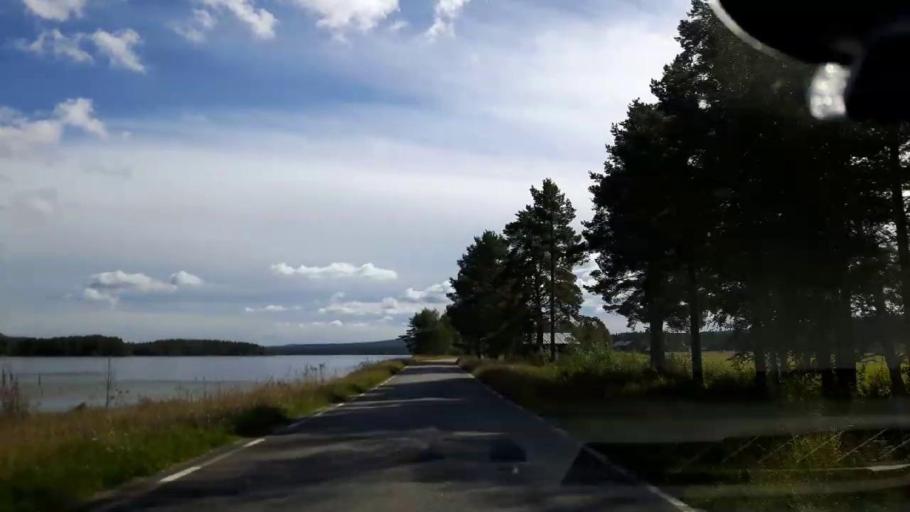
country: SE
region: Jaemtland
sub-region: Braecke Kommun
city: Braecke
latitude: 63.2123
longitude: 15.3462
